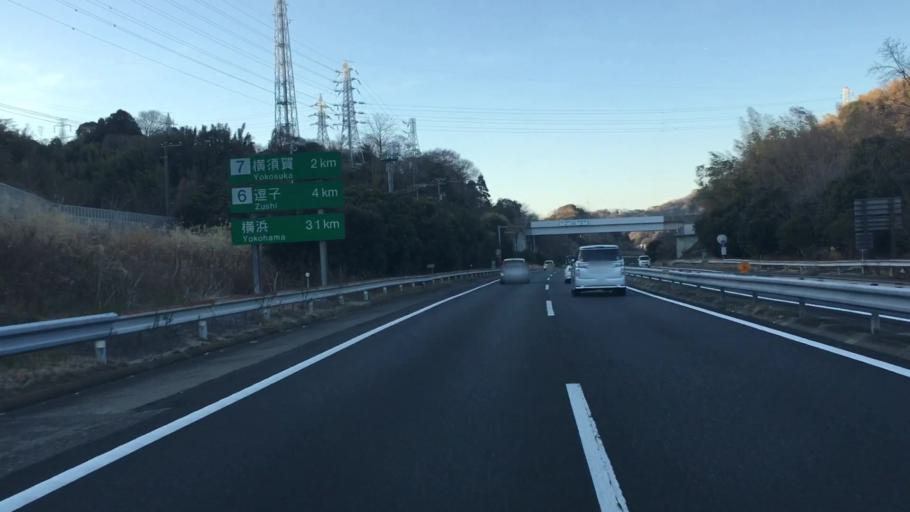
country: JP
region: Kanagawa
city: Yokosuka
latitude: 35.2572
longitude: 139.6355
